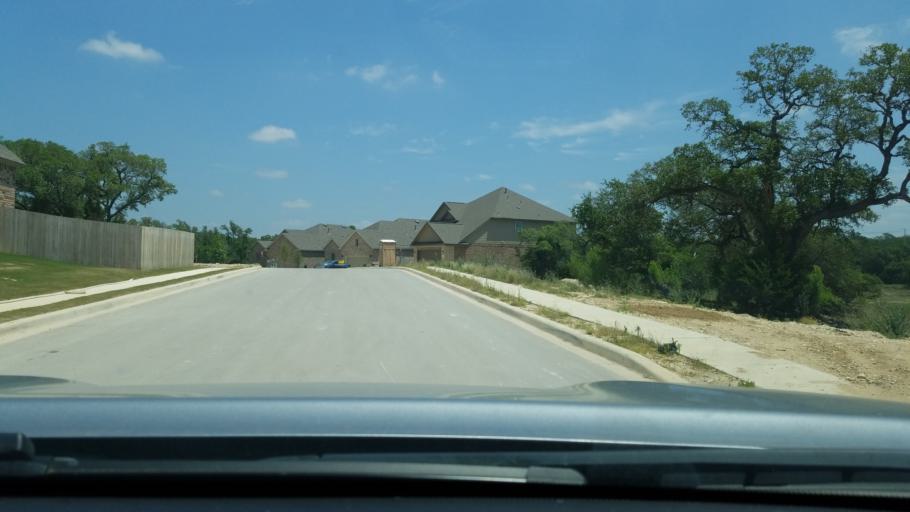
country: US
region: Texas
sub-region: Comal County
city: Bulverde
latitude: 29.7996
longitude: -98.5221
